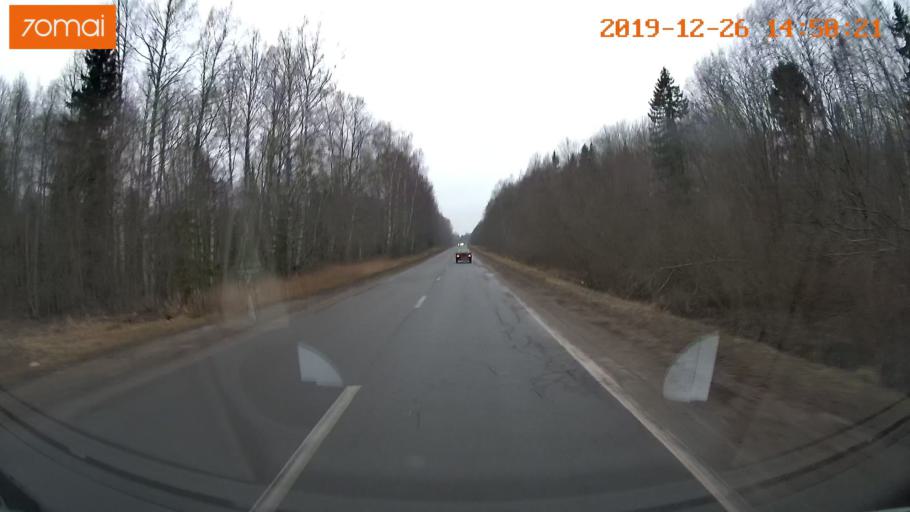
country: RU
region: Jaroslavl
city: Poshekhon'ye
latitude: 58.3326
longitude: 38.9273
